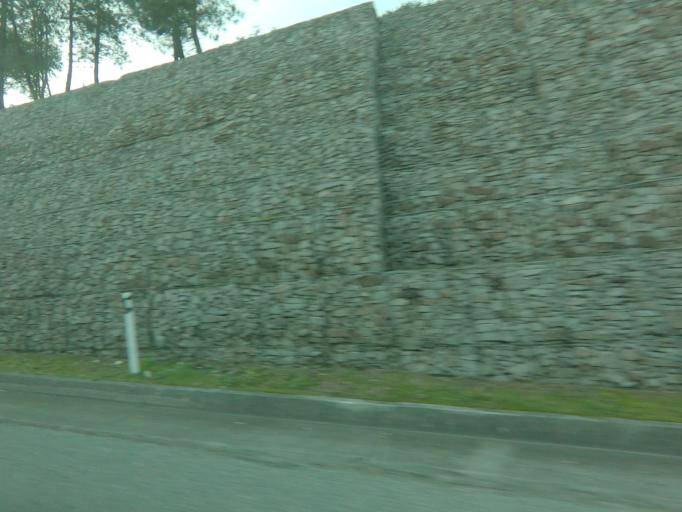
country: PT
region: Porto
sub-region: Lousada
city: Meinedo
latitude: 41.2307
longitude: -8.2247
